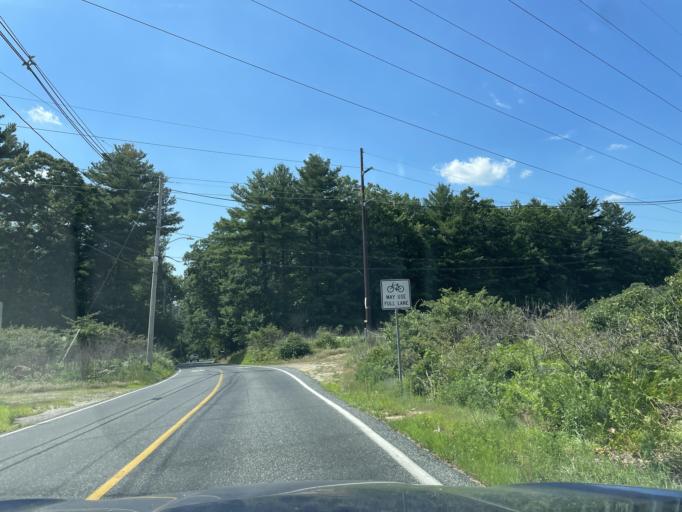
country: US
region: Massachusetts
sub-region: Middlesex County
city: Framingham
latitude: 42.2390
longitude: -71.4118
